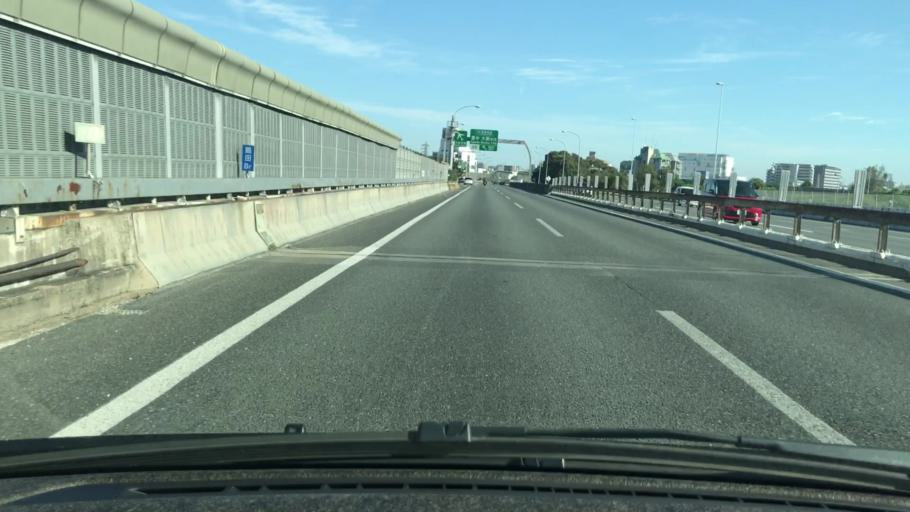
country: JP
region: Osaka
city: Toyonaka
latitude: 34.7523
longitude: 135.4626
